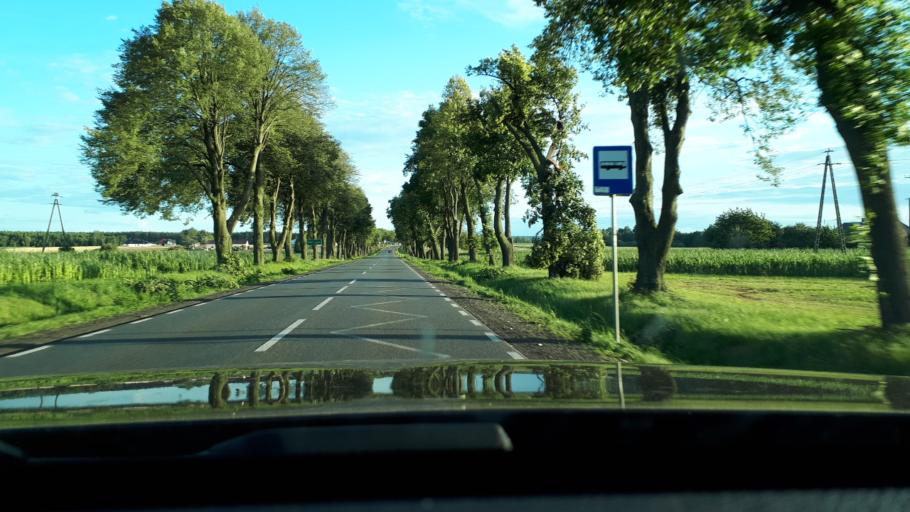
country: PL
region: Masovian Voivodeship
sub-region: Powiat ciechanowski
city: Ciechanow
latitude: 52.8257
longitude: 20.6168
